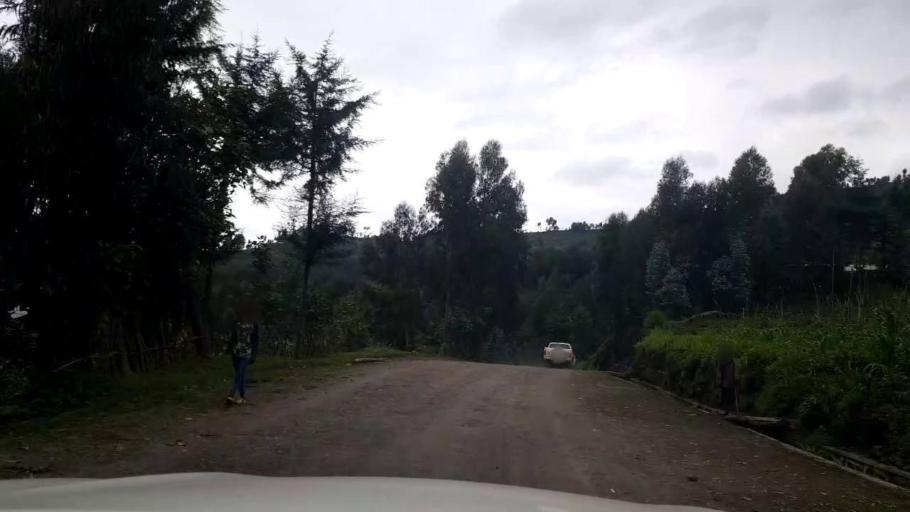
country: RW
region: Northern Province
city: Musanze
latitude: -1.5069
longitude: 29.5326
